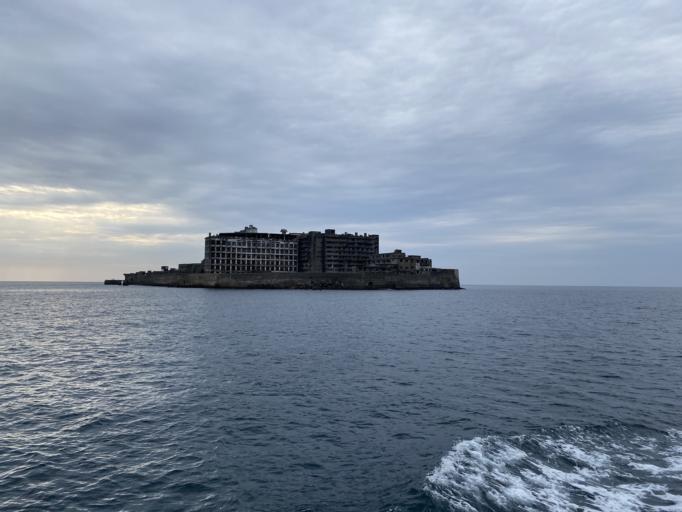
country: JP
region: Nagasaki
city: Nagasaki-shi
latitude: 32.6306
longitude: 129.7419
